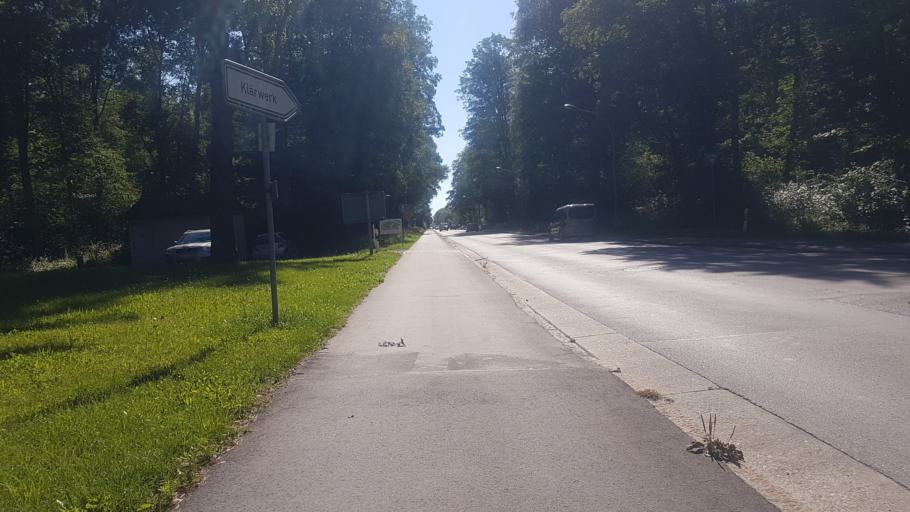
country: DE
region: Bavaria
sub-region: Upper Bavaria
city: Neuburg an der Donau
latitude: 48.7375
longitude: 11.2019
